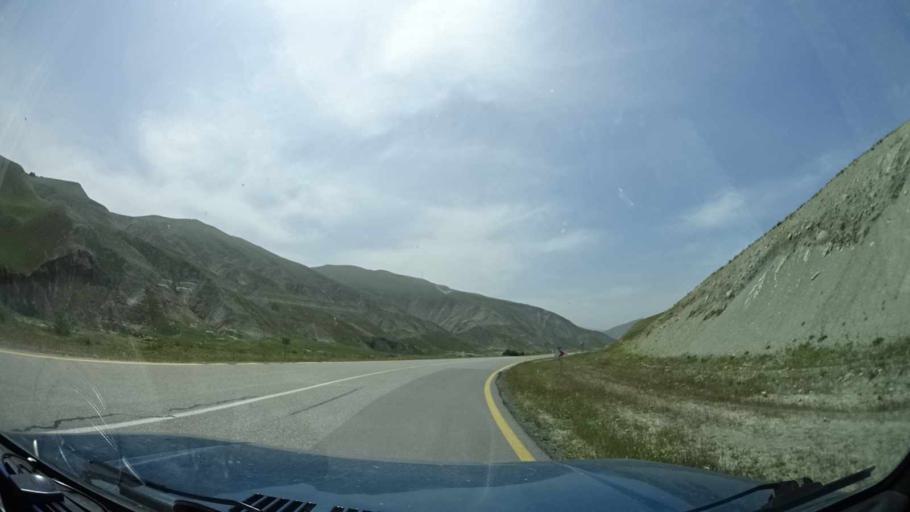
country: AZ
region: Xizi
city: Kilyazi
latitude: 40.8511
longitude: 49.3086
